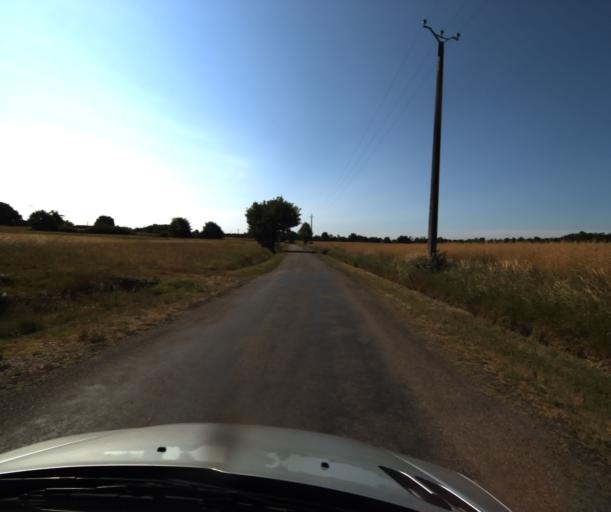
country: FR
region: Midi-Pyrenees
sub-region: Departement du Tarn-et-Garonne
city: Bressols
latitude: 43.9444
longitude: 1.2960
